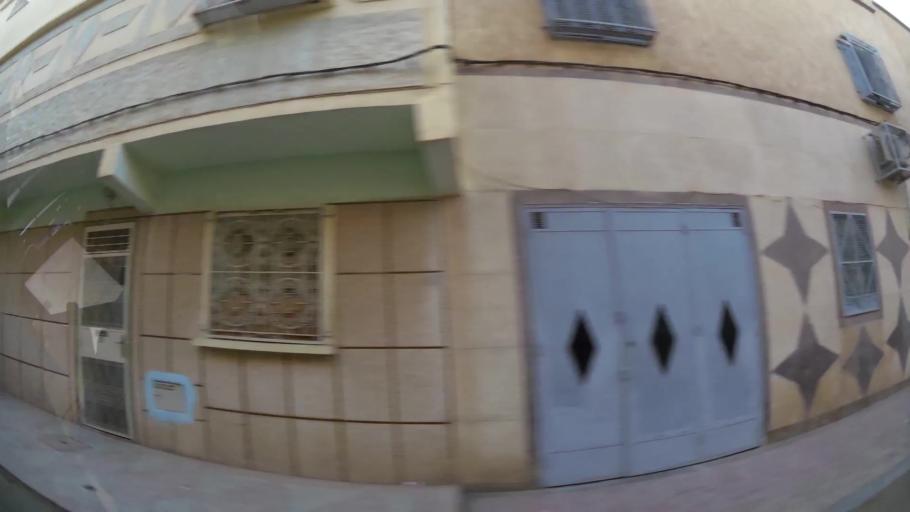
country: MA
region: Oriental
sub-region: Oujda-Angad
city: Oujda
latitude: 34.7041
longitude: -1.9134
